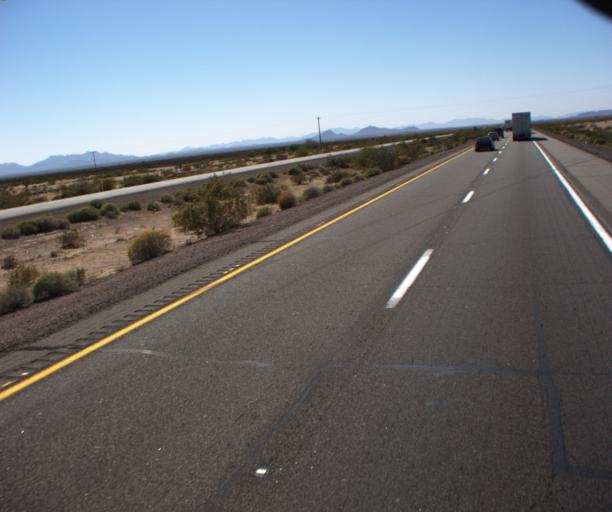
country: US
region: Arizona
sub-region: Yuma County
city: Wellton
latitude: 32.7175
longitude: -113.7967
